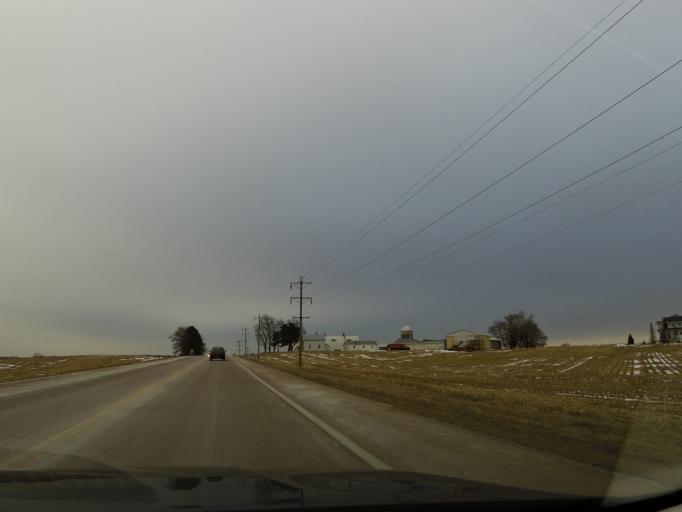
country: US
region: Minnesota
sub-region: Carver County
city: Watertown
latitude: 44.9152
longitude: -93.8279
